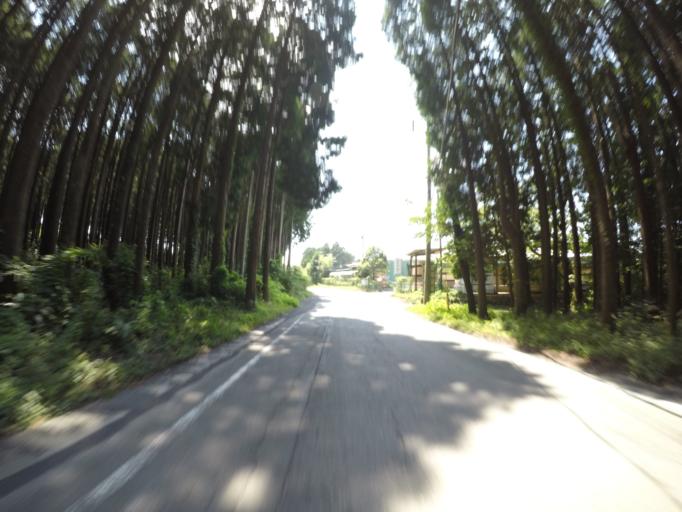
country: JP
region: Shizuoka
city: Fuji
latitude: 35.2347
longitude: 138.6919
